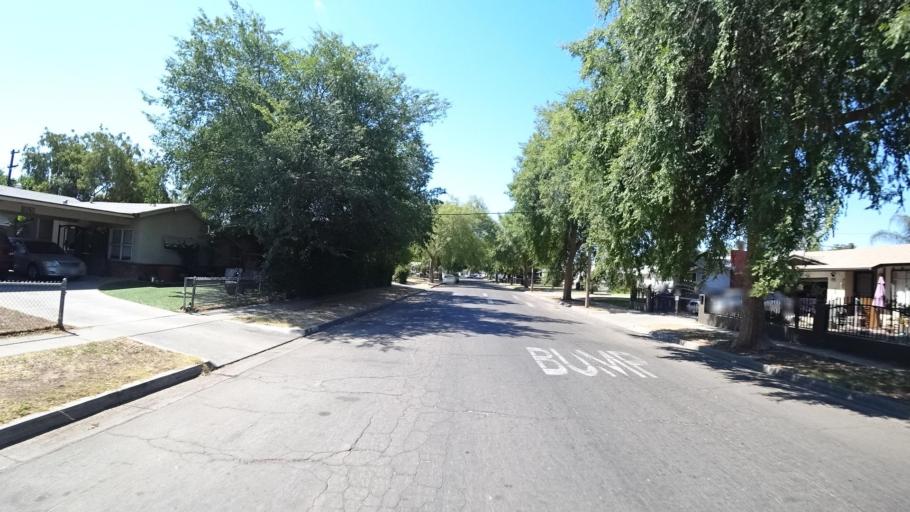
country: US
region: California
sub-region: Fresno County
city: Fresno
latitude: 36.7273
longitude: -119.7406
